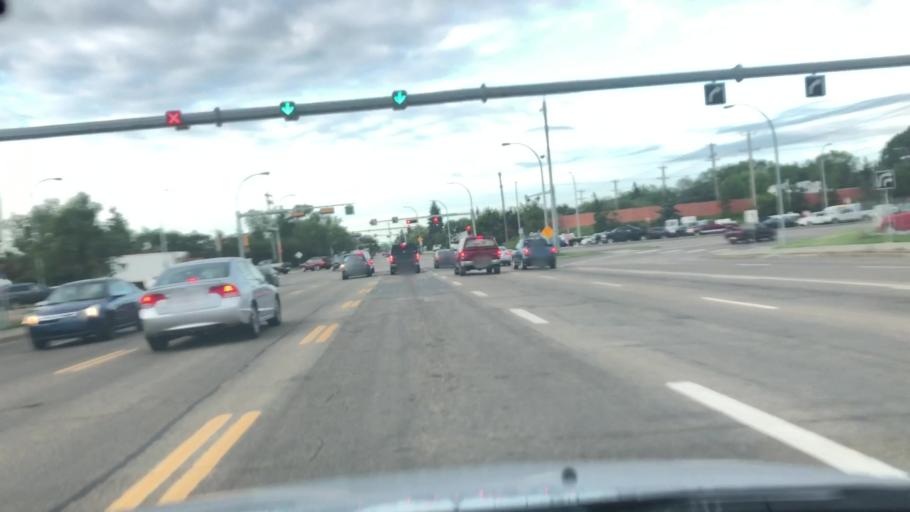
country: CA
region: Alberta
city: Edmonton
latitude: 53.5816
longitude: -113.5411
